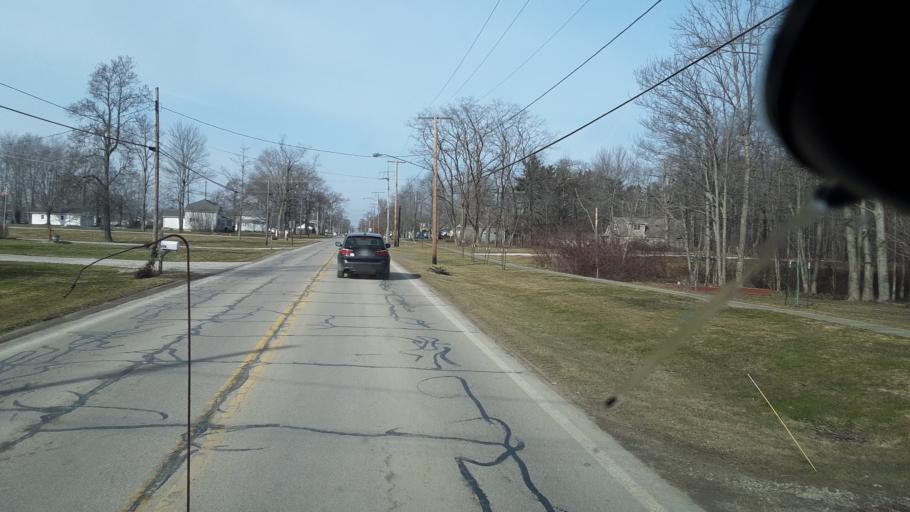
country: US
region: Ohio
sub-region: Ashtabula County
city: Jefferson
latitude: 41.7384
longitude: -80.7523
